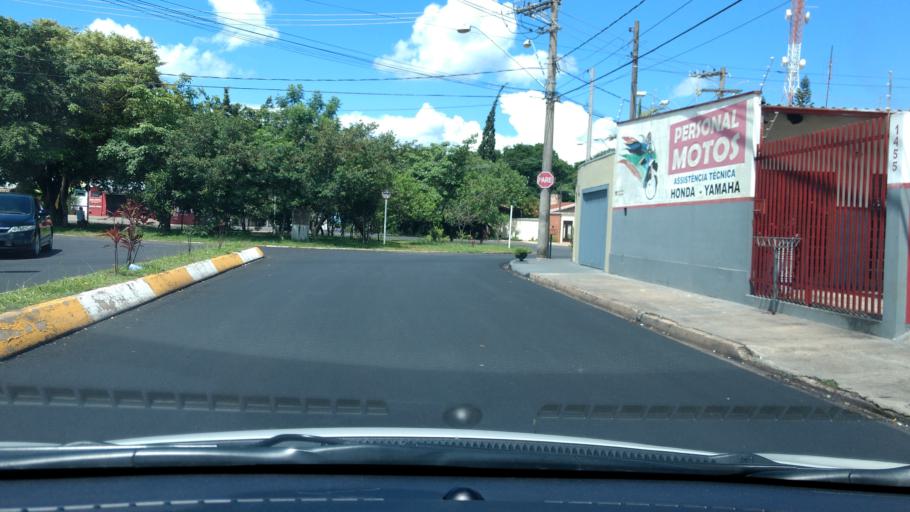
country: BR
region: Sao Paulo
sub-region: Botucatu
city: Botucatu
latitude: -22.8633
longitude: -48.4472
